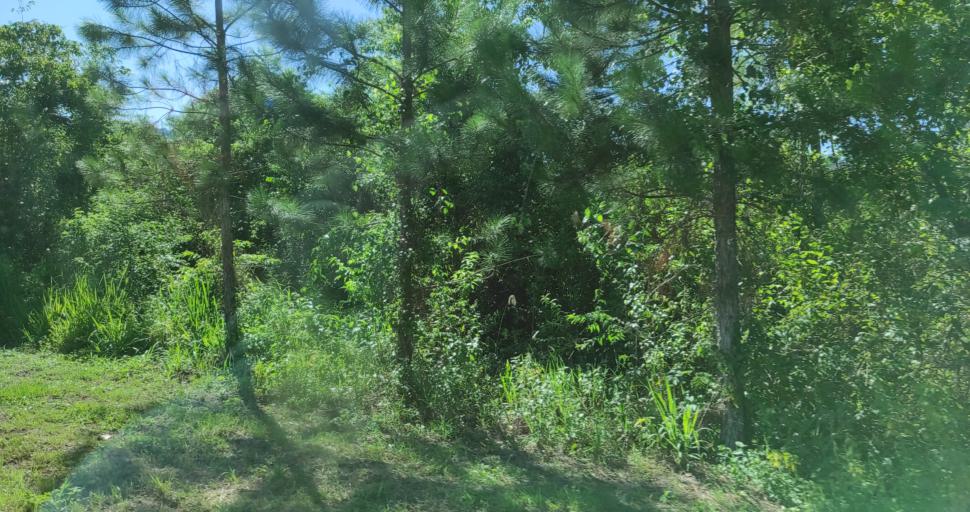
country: AR
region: Misiones
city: El Soberbio
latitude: -27.2459
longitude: -54.0265
